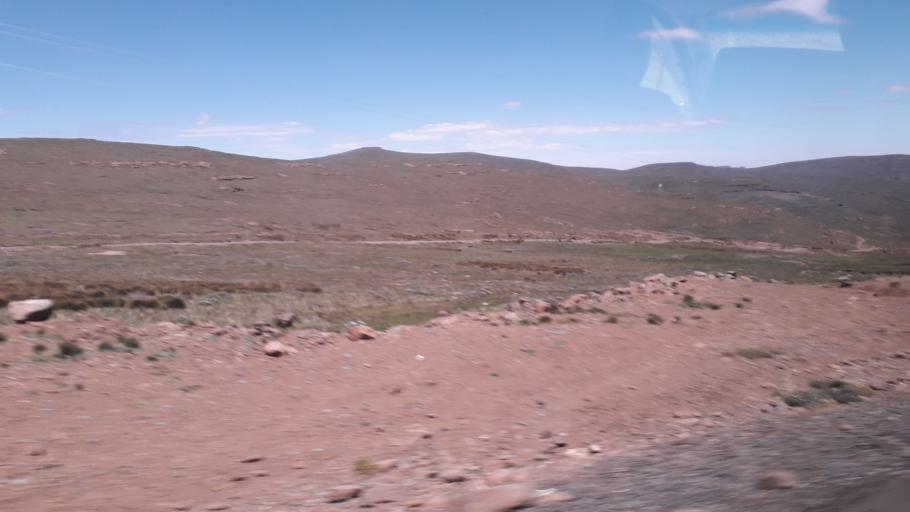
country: ZA
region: Orange Free State
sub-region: Thabo Mofutsanyana District Municipality
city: Phuthaditjhaba
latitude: -28.8150
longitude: 28.7178
